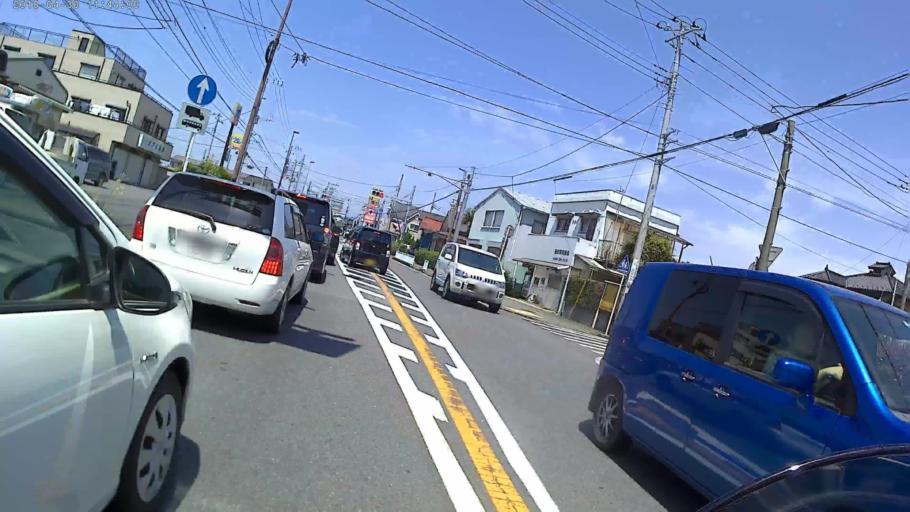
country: JP
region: Kanagawa
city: Zama
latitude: 35.4865
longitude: 139.3914
